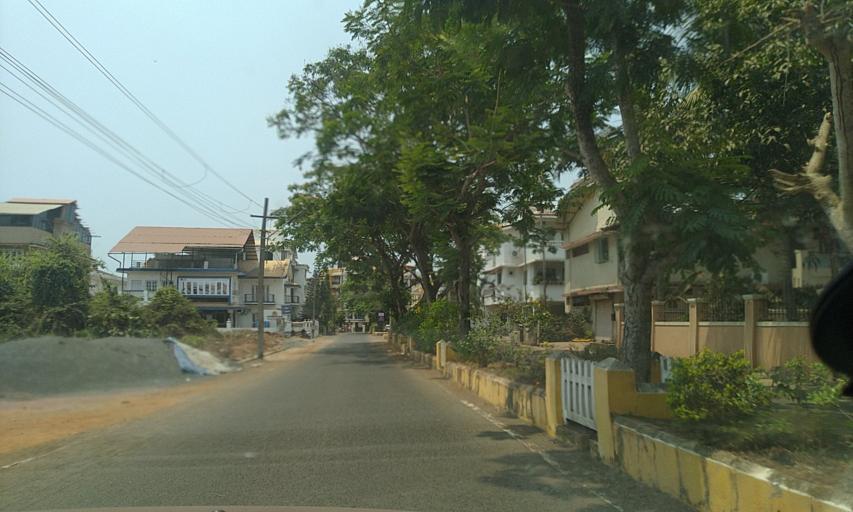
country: IN
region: Goa
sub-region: North Goa
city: Panaji
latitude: 15.5223
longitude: 73.8218
